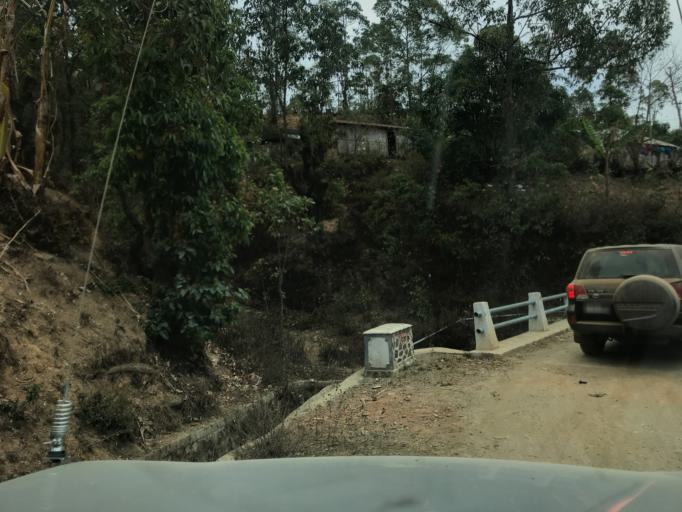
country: TL
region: Ermera
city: Gleno
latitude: -8.8383
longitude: 125.4419
